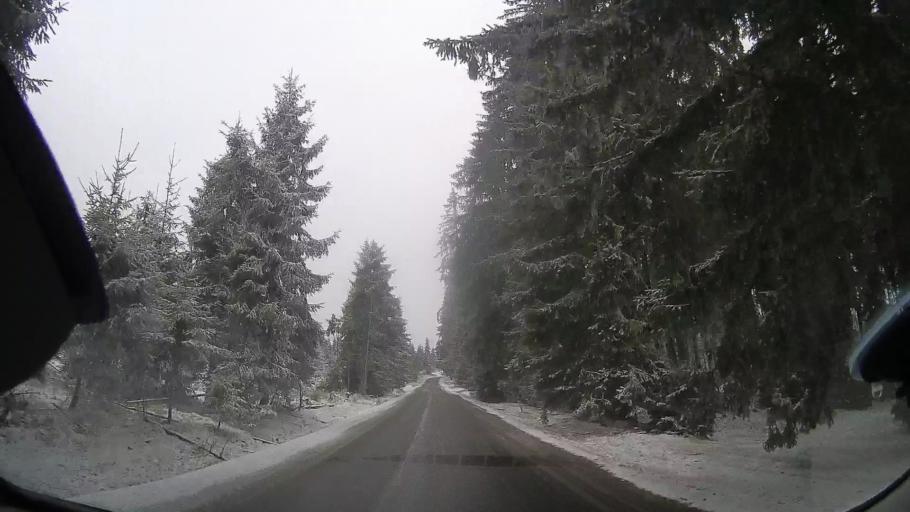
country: RO
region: Cluj
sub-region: Comuna Belis
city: Belis
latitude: 46.6398
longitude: 23.0566
